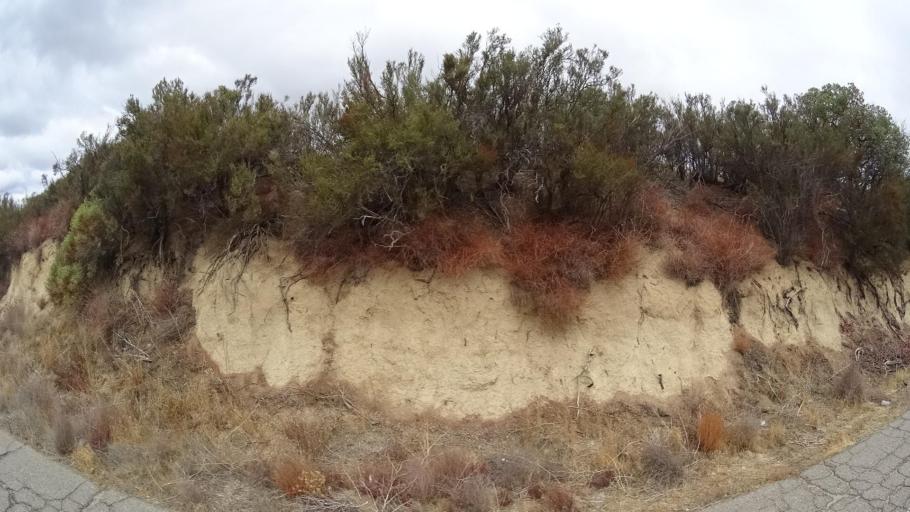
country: US
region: California
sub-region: San Diego County
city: Campo
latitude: 32.7197
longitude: -116.3992
